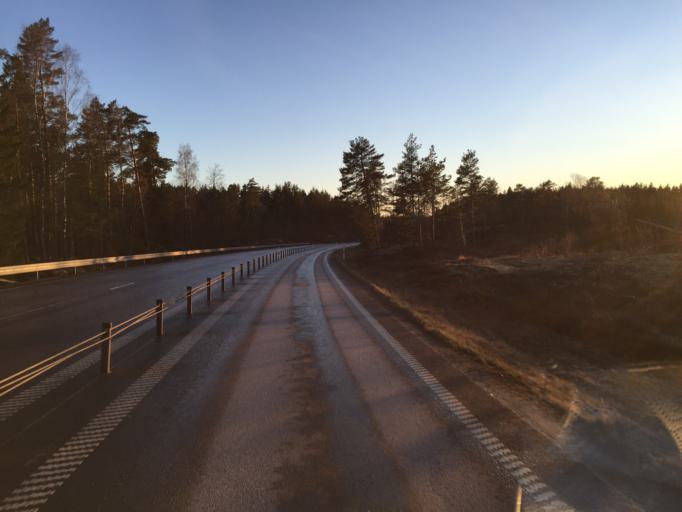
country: SE
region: Kalmar
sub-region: Vasterviks Kommun
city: Forserum
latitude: 57.9698
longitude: 16.4769
